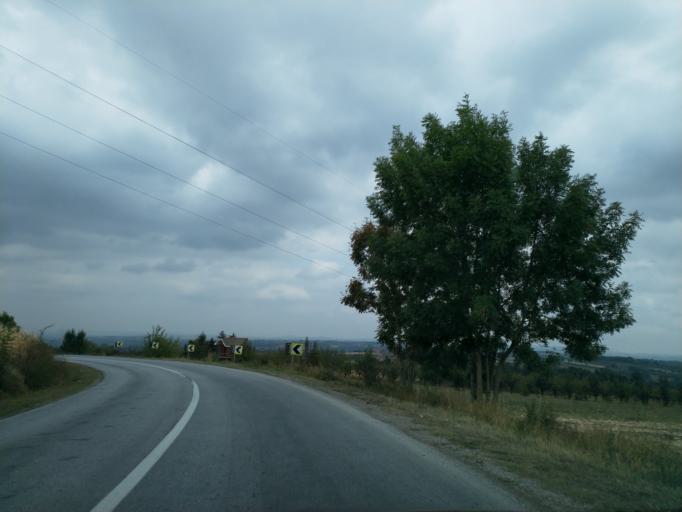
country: RS
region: Central Serbia
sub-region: Sumadijski Okrug
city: Topola
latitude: 44.1659
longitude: 20.7385
